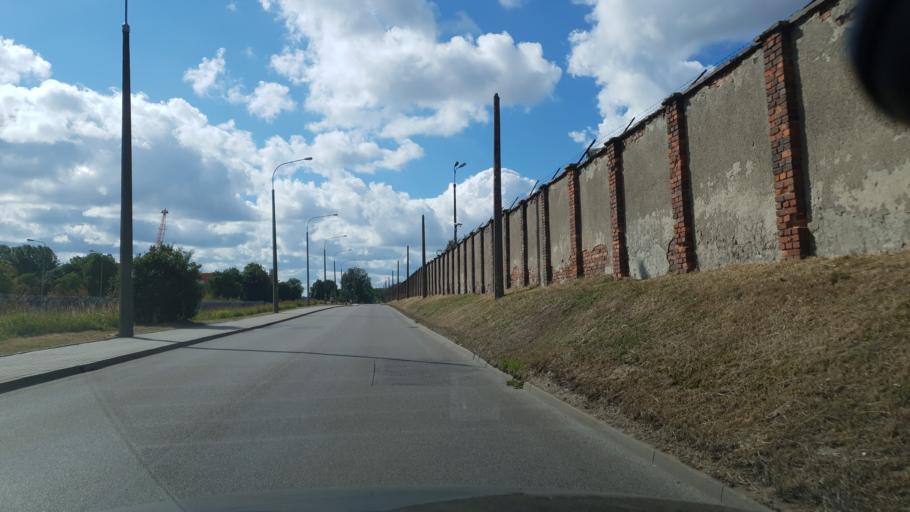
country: PL
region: Pomeranian Voivodeship
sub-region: Gdynia
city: Gdynia
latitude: 54.5444
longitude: 18.5256
